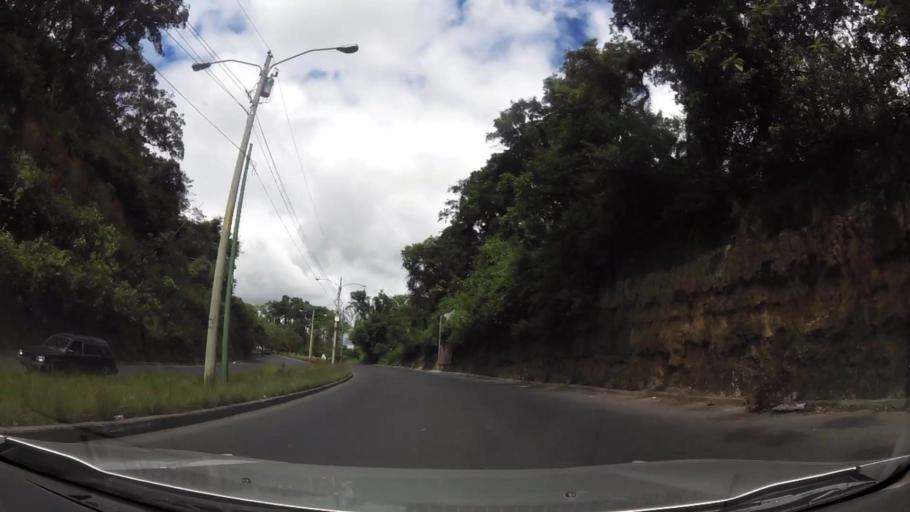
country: GT
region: Guatemala
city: Guatemala City
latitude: 14.6548
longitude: -90.5485
